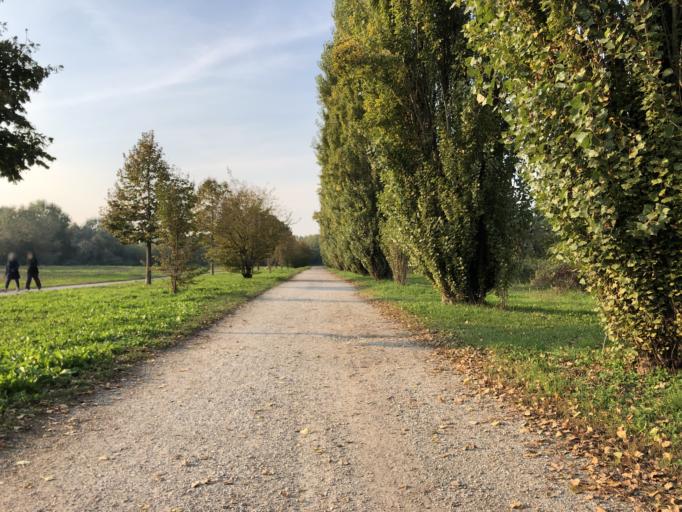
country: IT
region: Lombardy
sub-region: Citta metropolitana di Milano
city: Chiaravalle
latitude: 45.4257
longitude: 9.2259
